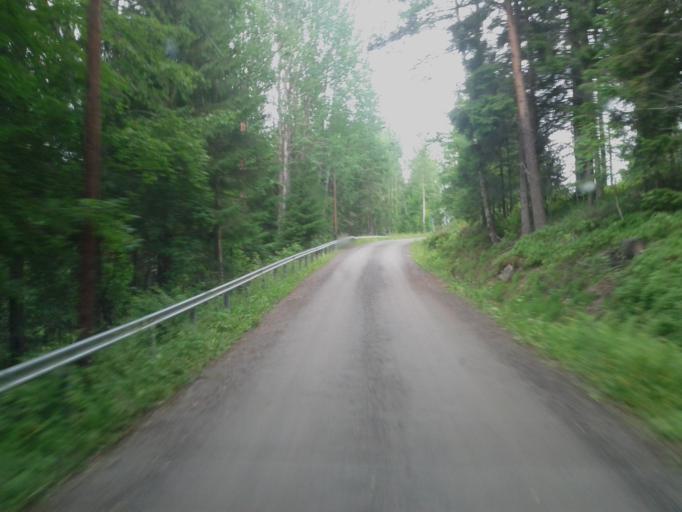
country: SE
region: Vaesternorrland
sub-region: OErnskoeldsviks Kommun
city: Bjasta
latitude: 63.0678
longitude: 18.4266
